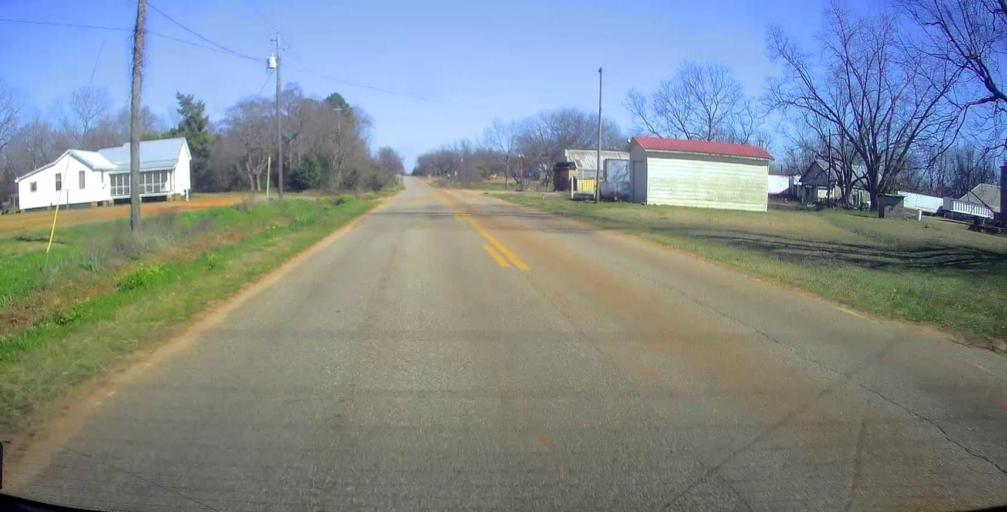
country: US
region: Georgia
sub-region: Peach County
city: Fort Valley
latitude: 32.6119
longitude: -83.9789
